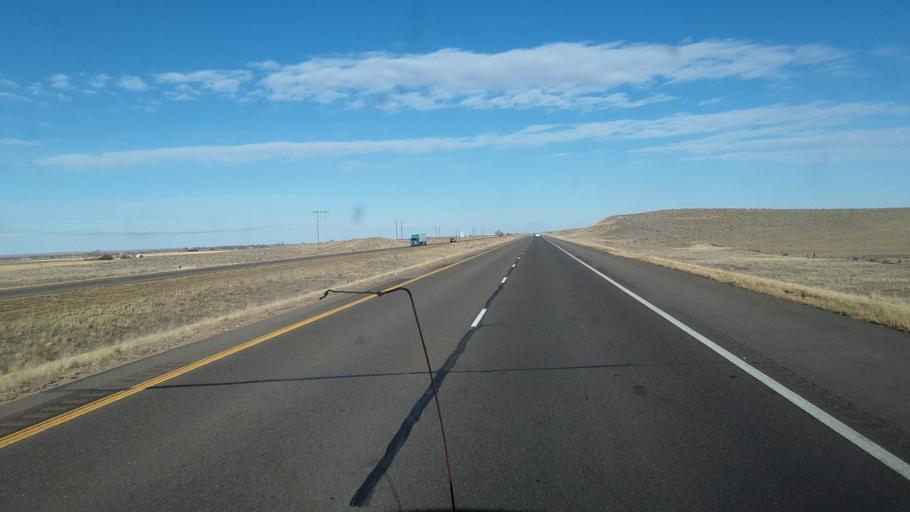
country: US
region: Colorado
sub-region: Morgan County
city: Brush
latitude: 40.2908
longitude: -103.5453
